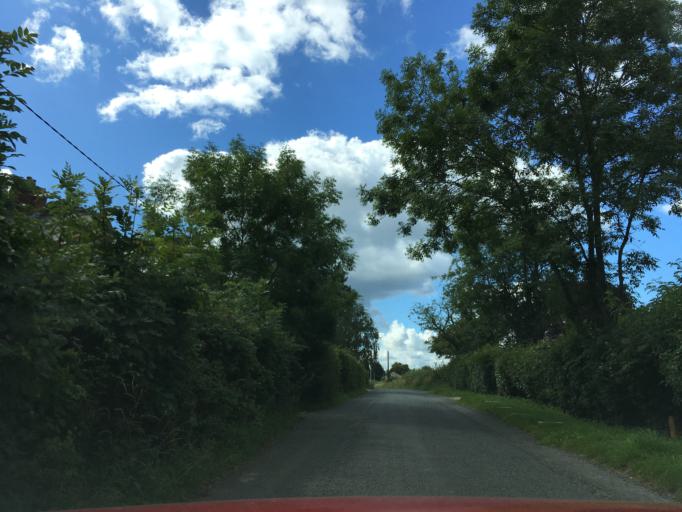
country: GB
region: England
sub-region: Gloucestershire
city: Newent
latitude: 51.8573
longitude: -2.3532
